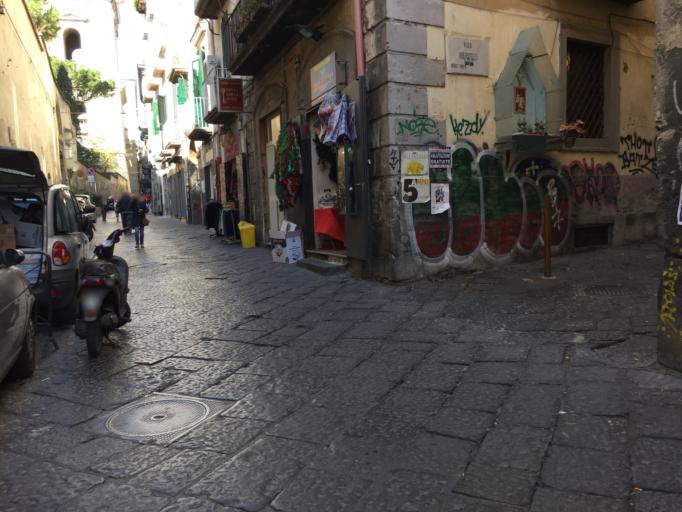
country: IT
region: Campania
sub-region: Provincia di Napoli
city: Napoli
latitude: 40.8466
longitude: 14.2537
